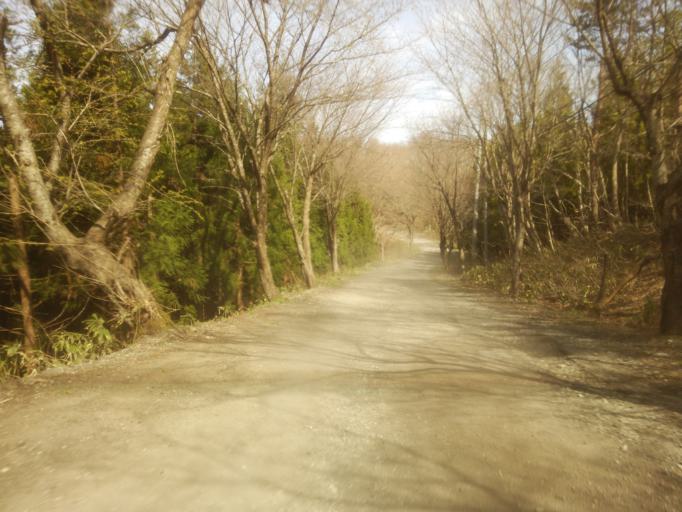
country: JP
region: Fukushima
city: Inawashiro
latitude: 37.5277
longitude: 140.0340
